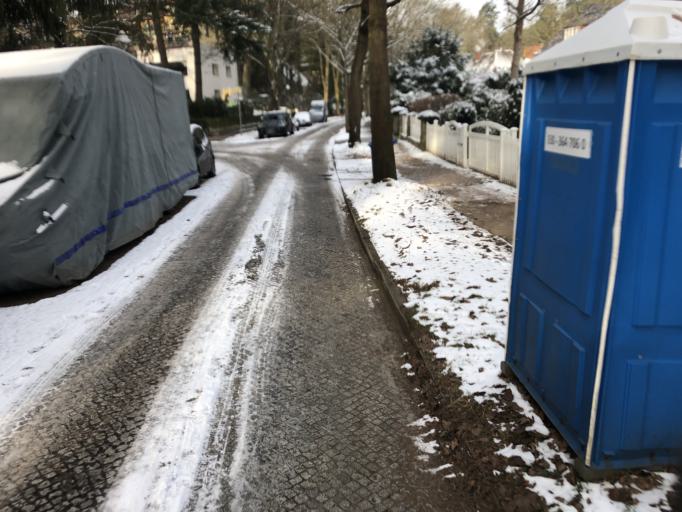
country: DE
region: Berlin
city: Frohnau
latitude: 52.6286
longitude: 13.2995
